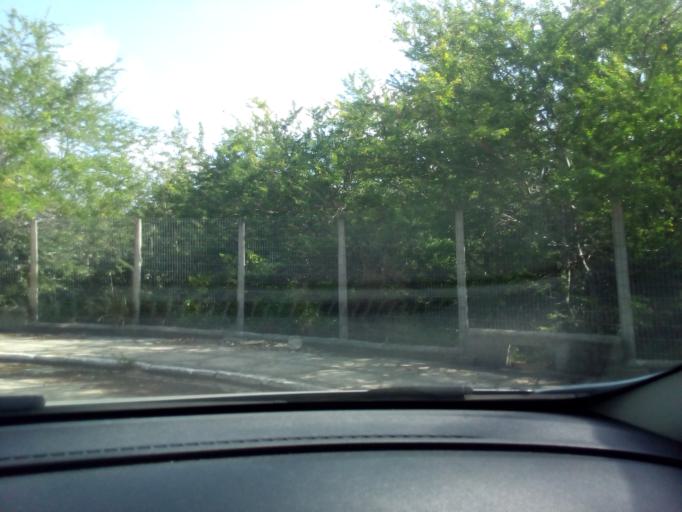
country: BR
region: Rio Grande do Norte
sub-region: Natal
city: Natal
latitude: -5.8419
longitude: -35.2011
